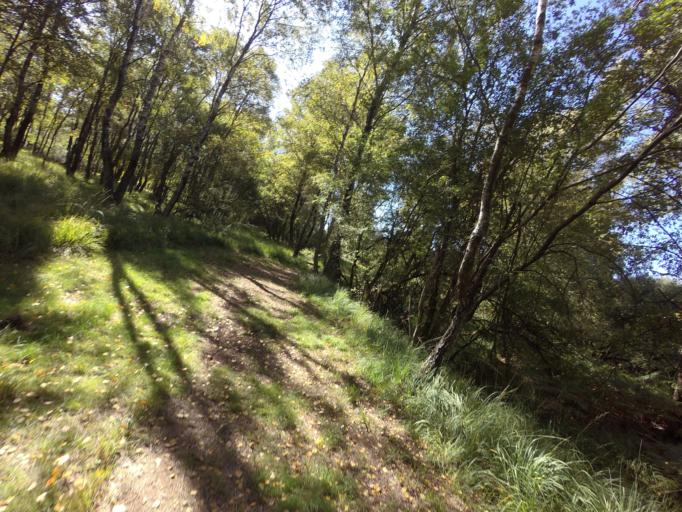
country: DE
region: North Rhine-Westphalia
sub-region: Regierungsbezirk Koln
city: Roetgen
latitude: 50.6001
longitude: 6.1558
